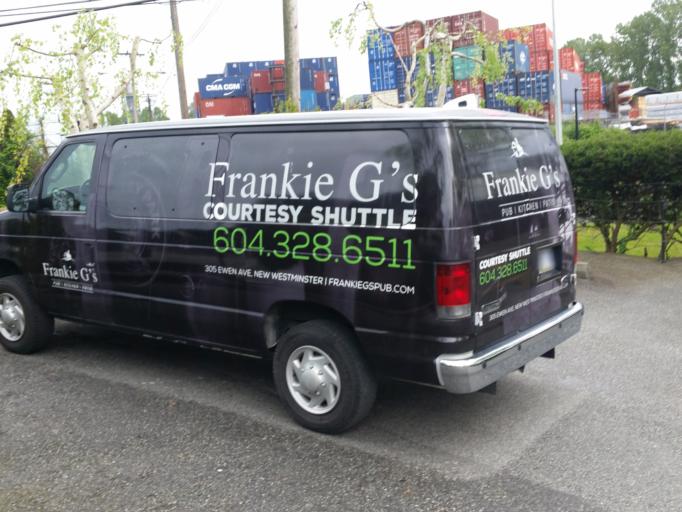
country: CA
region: British Columbia
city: New Westminster
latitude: 49.1934
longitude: -122.9304
